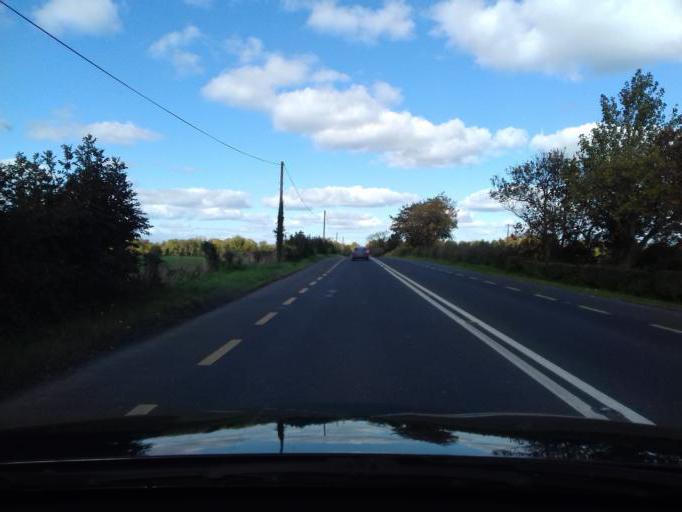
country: IE
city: Kentstown
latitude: 53.6685
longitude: -6.5316
